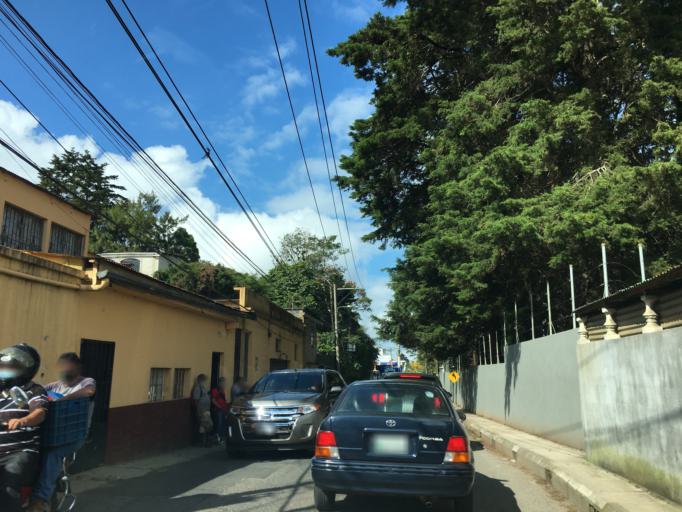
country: GT
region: Guatemala
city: San Jose Pinula
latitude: 14.5645
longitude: -90.4379
